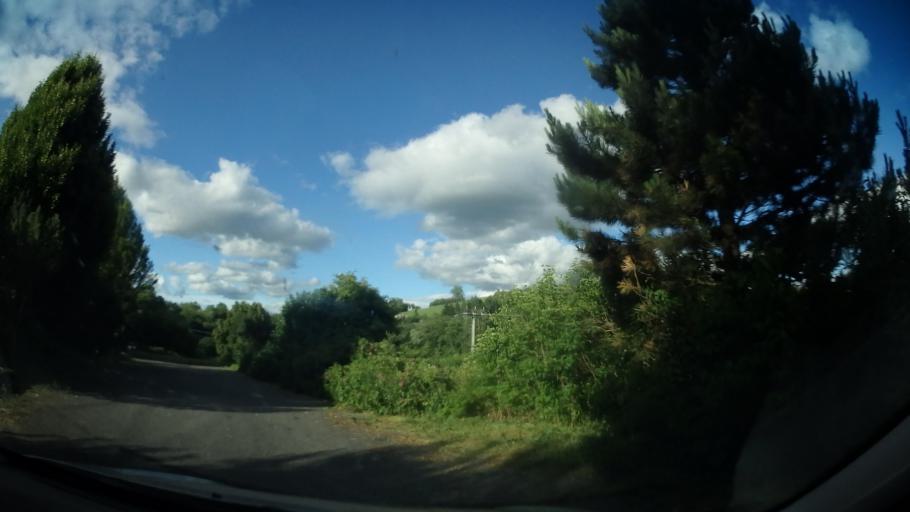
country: CZ
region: Vysocina
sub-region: Okres Zd'ar nad Sazavou
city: Nove Mesto na Morave
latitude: 49.6284
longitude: 16.1123
